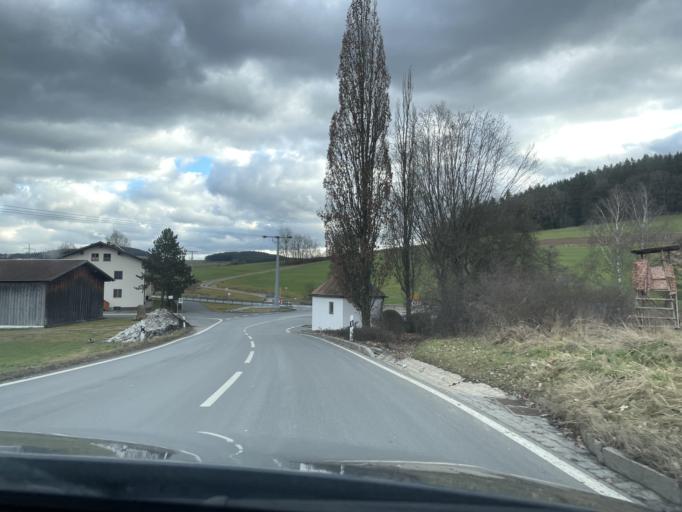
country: DE
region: Bavaria
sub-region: Upper Palatinate
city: Runding
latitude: 49.2032
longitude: 12.7761
